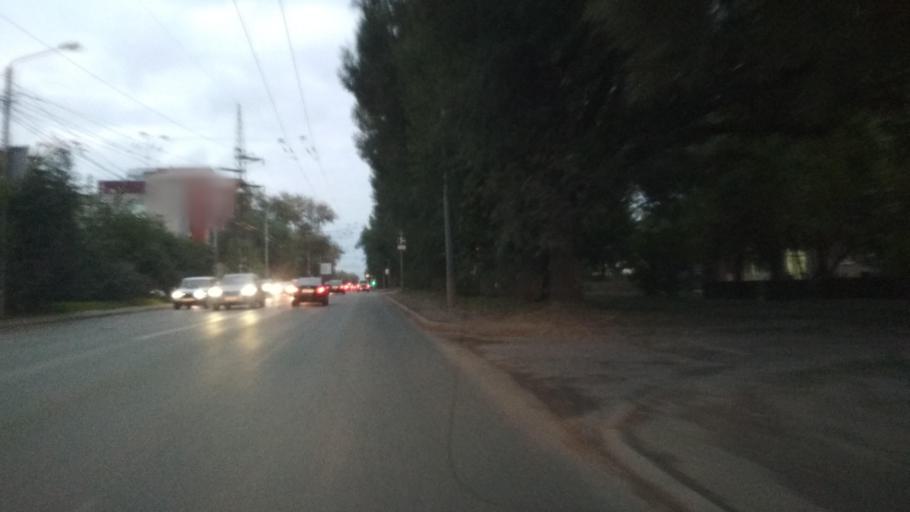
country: RU
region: Tomsk
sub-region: Tomskiy Rayon
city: Tomsk
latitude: 56.4760
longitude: 84.9944
